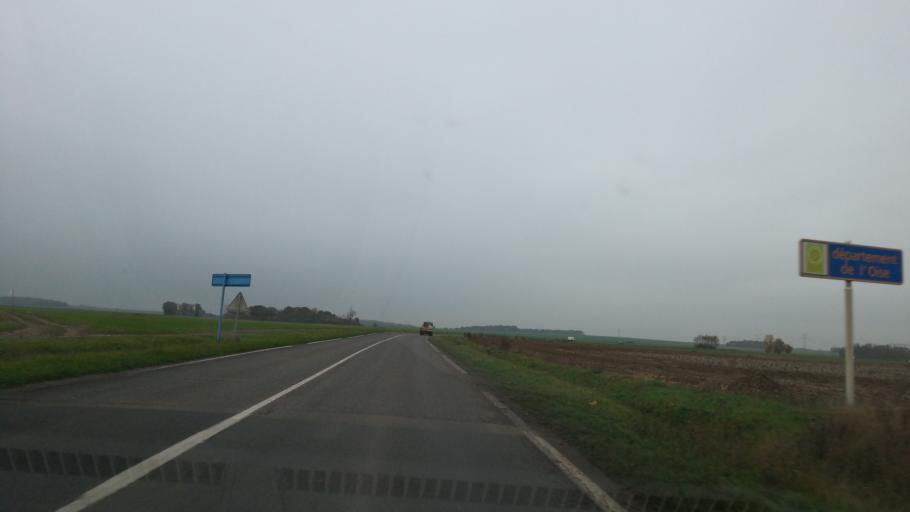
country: FR
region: Picardie
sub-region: Departement de l'Oise
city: Boran-sur-Oise
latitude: 49.1636
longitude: 2.3437
